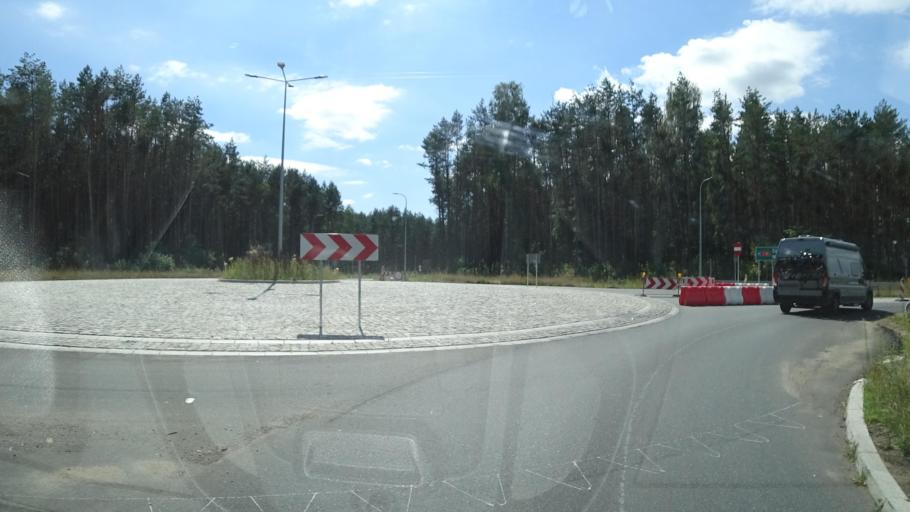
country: PL
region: Podlasie
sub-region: Powiat grajewski
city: Szczuczyn
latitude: 53.5891
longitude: 22.3382
